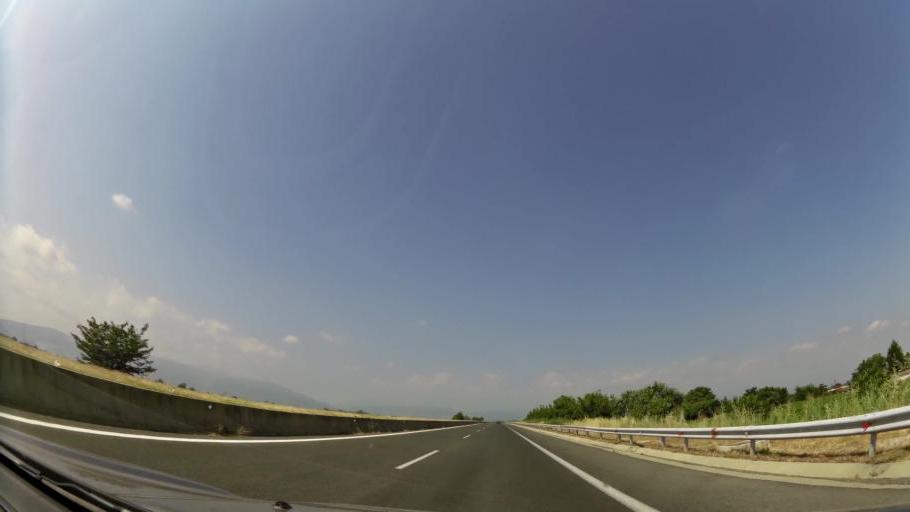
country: GR
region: Central Macedonia
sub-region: Nomos Imathias
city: Kouloura
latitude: 40.5585
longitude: 22.3548
